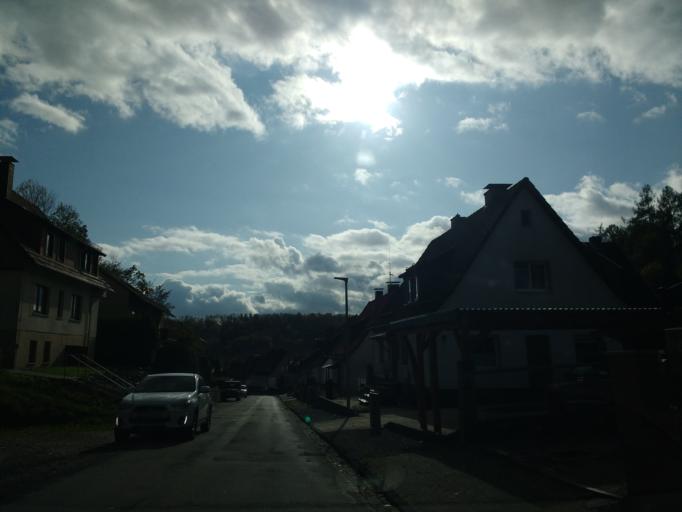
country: DE
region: Lower Saxony
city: Herzberg am Harz
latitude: 51.6324
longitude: 10.3860
